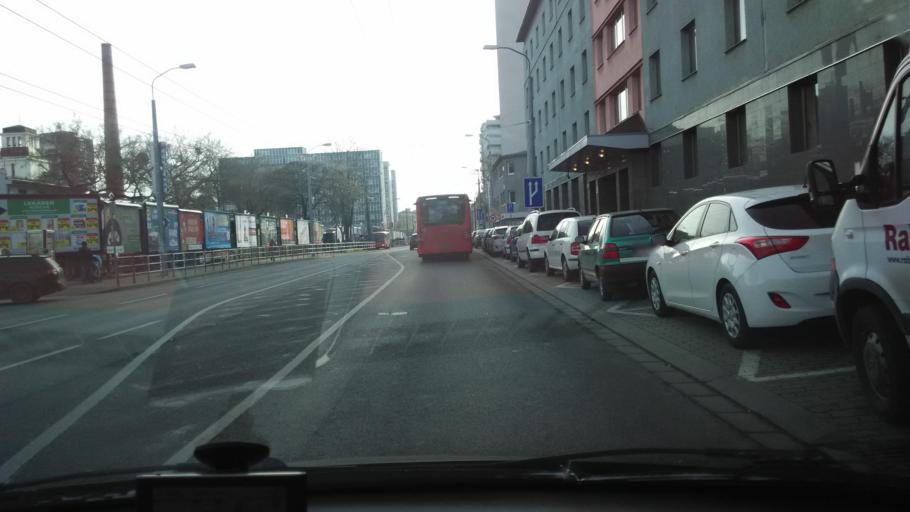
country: SK
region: Bratislavsky
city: Bratislava
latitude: 48.1545
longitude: 17.1343
